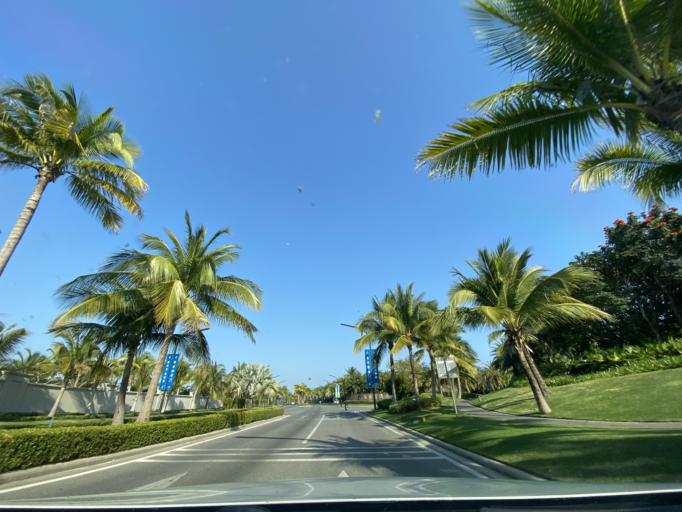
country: CN
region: Hainan
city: Xincun
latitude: 18.4218
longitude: 109.9474
